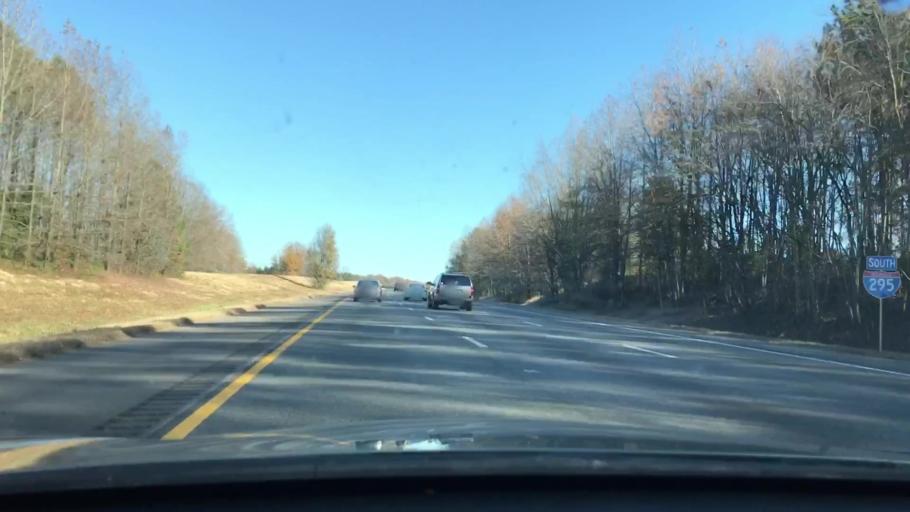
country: US
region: Virginia
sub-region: Henrico County
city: Glen Allen
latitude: 37.6818
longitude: -77.5300
